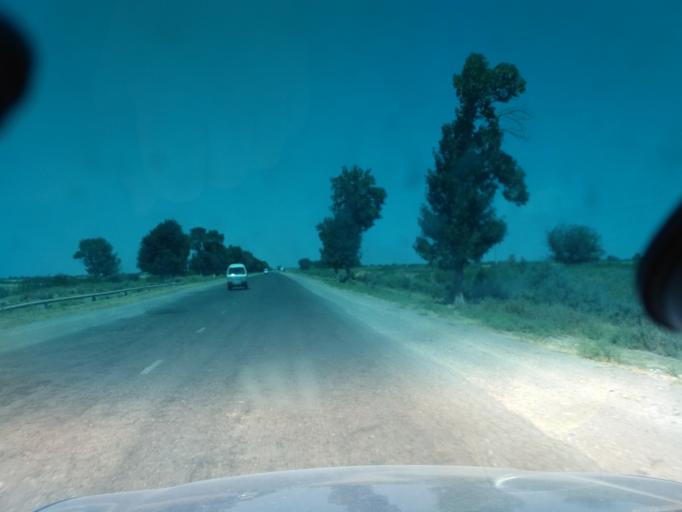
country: UZ
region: Sirdaryo
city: Guliston
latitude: 40.5023
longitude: 68.9519
